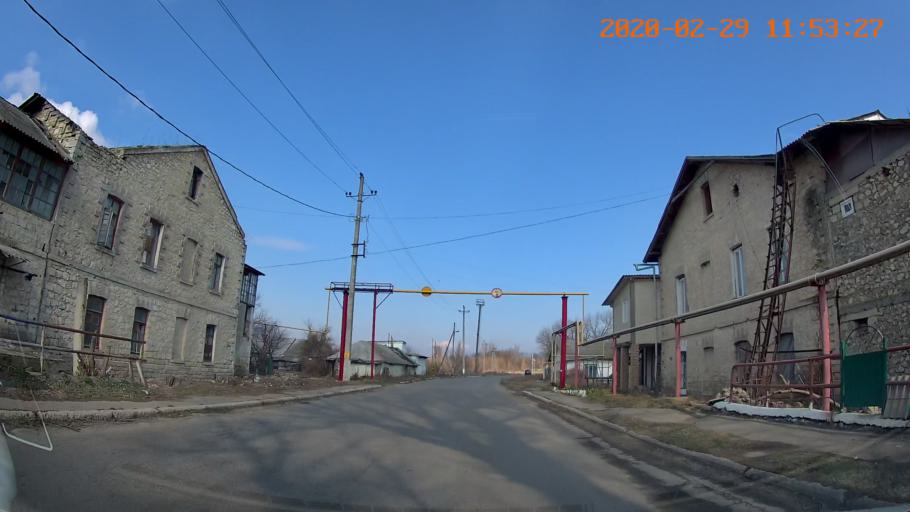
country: MD
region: Telenesti
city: Ribnita
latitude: 47.7777
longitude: 28.9909
